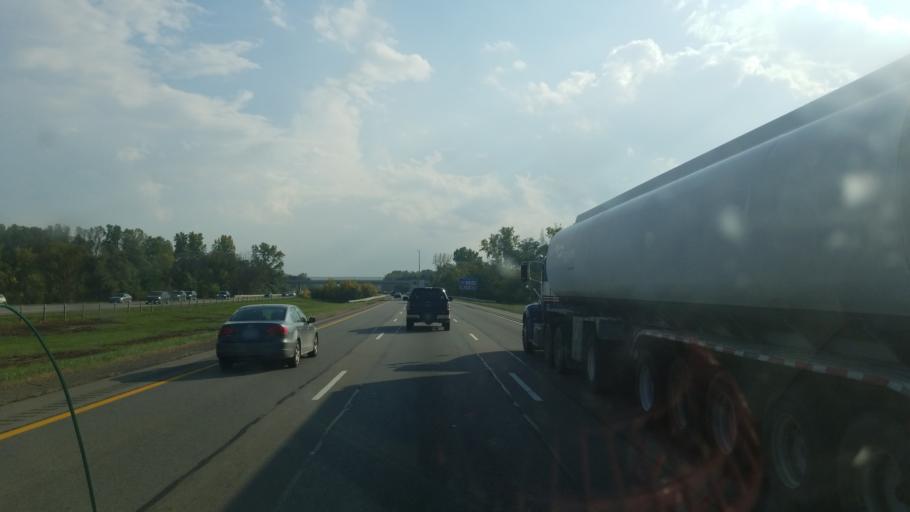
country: US
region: Michigan
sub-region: Wayne County
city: Plymouth
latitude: 42.3378
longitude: -83.4434
